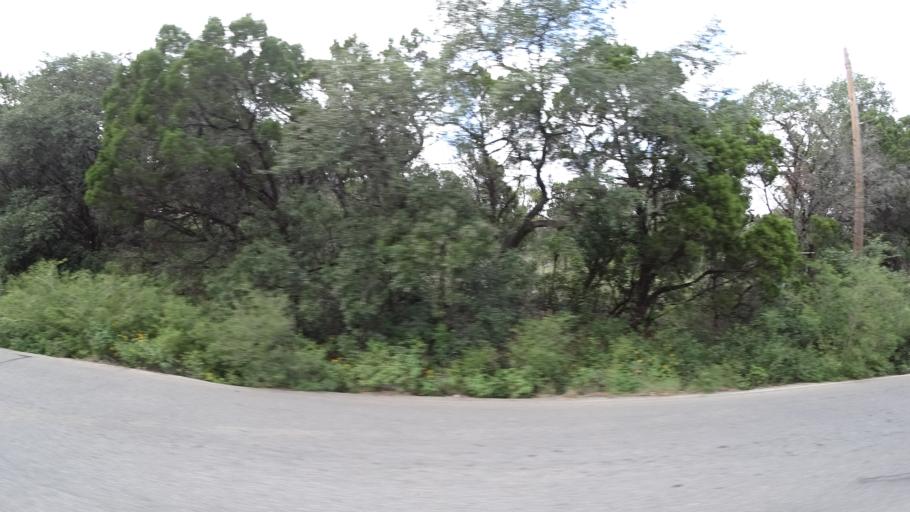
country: US
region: Texas
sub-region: Travis County
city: West Lake Hills
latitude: 30.2928
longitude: -97.7977
